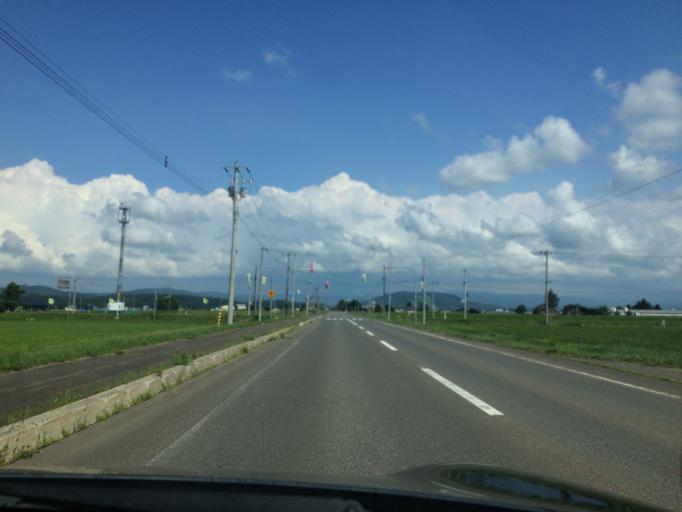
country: JP
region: Hokkaido
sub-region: Asahikawa-shi
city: Asahikawa
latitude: 43.7432
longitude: 142.4589
